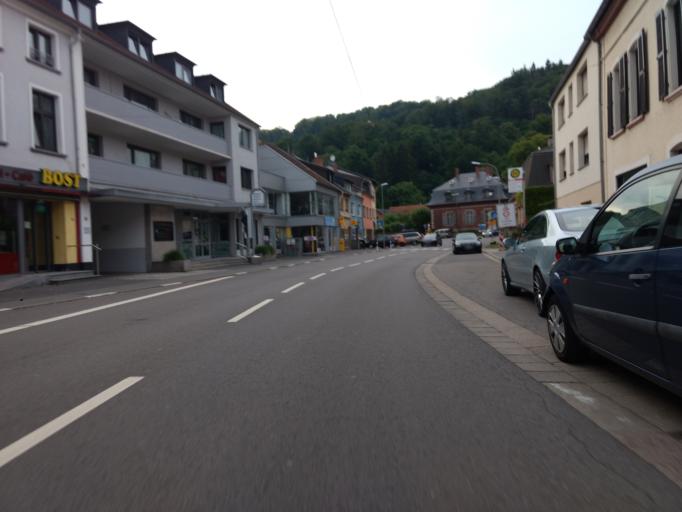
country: DE
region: Saarland
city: Wallerfangen
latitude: 49.3306
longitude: 6.7159
